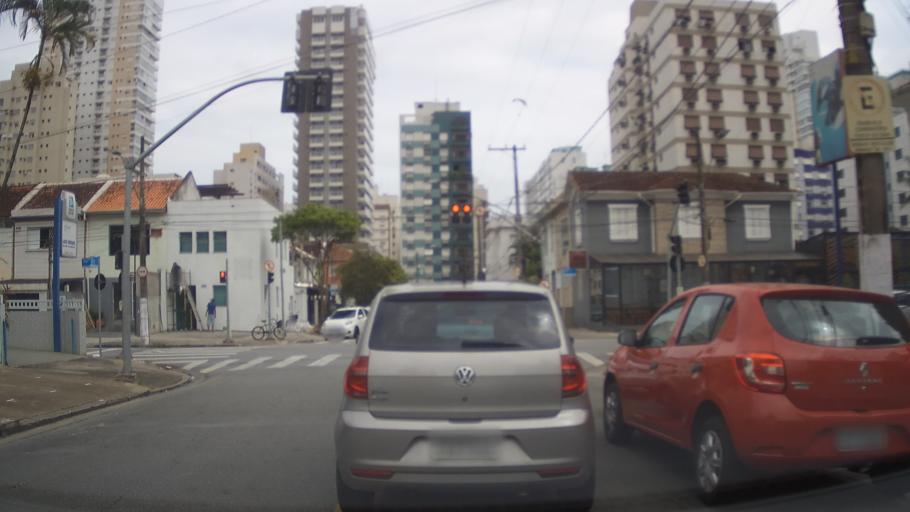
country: BR
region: Sao Paulo
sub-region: Santos
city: Santos
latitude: -23.9743
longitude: -46.3148
